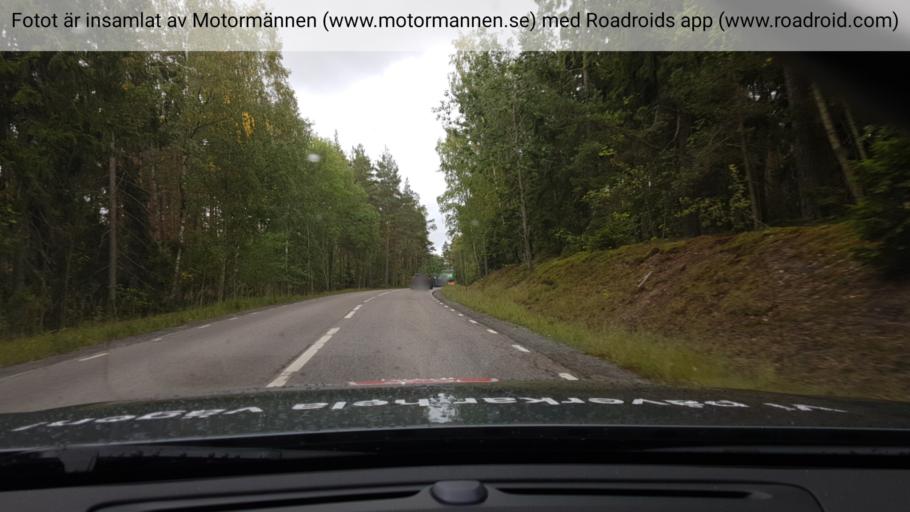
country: SE
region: Stockholm
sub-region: Botkyrka Kommun
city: Tullinge
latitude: 59.1620
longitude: 17.9261
